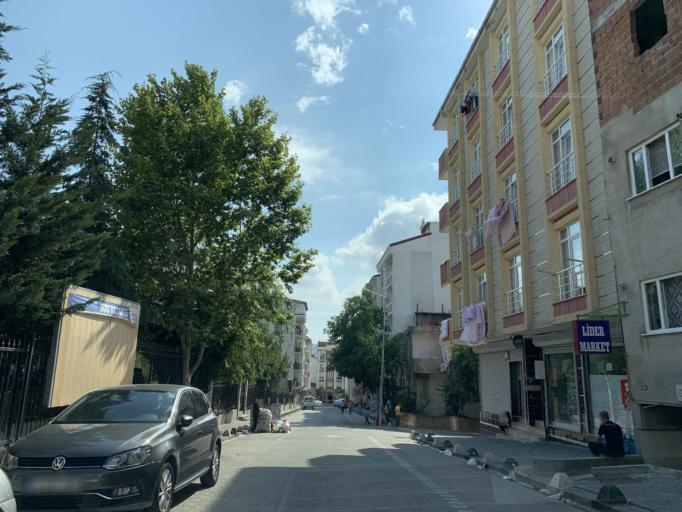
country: TR
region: Istanbul
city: Esenyurt
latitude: 41.0346
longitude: 28.6709
